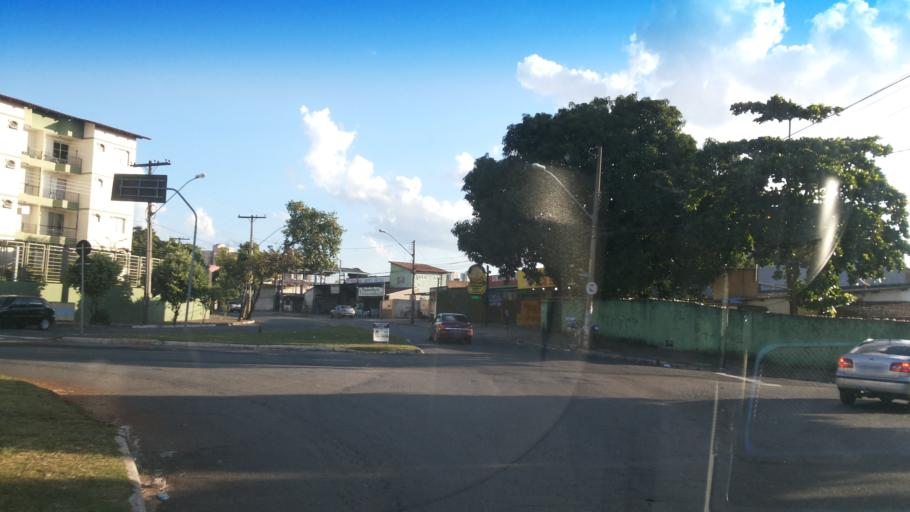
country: BR
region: Goias
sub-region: Goiania
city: Goiania
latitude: -16.6633
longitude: -49.2663
